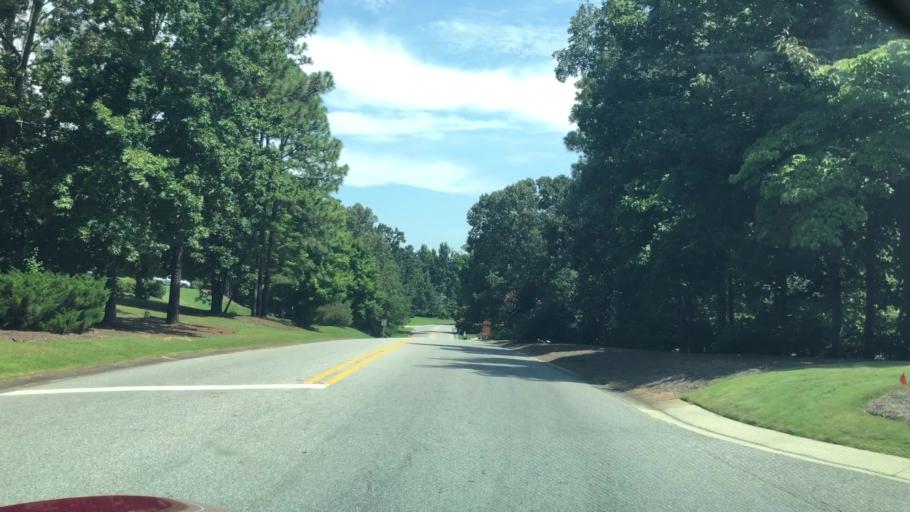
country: US
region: Alabama
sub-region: Shelby County
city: Meadowbrook
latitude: 33.4077
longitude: -86.6939
